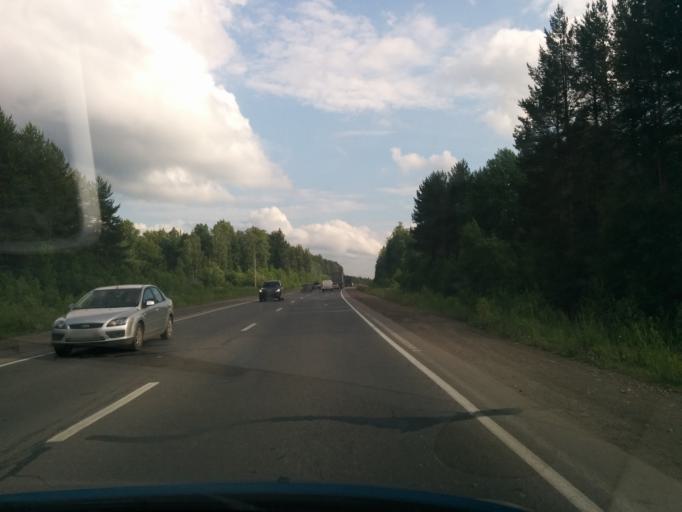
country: RU
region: Perm
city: Polazna
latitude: 58.1245
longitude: 56.4234
